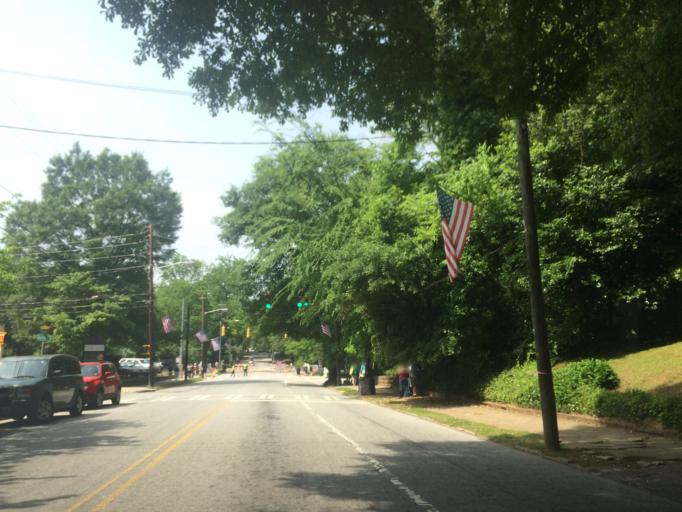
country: US
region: Georgia
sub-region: DeKalb County
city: Druid Hills
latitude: 33.7630
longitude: -84.3523
